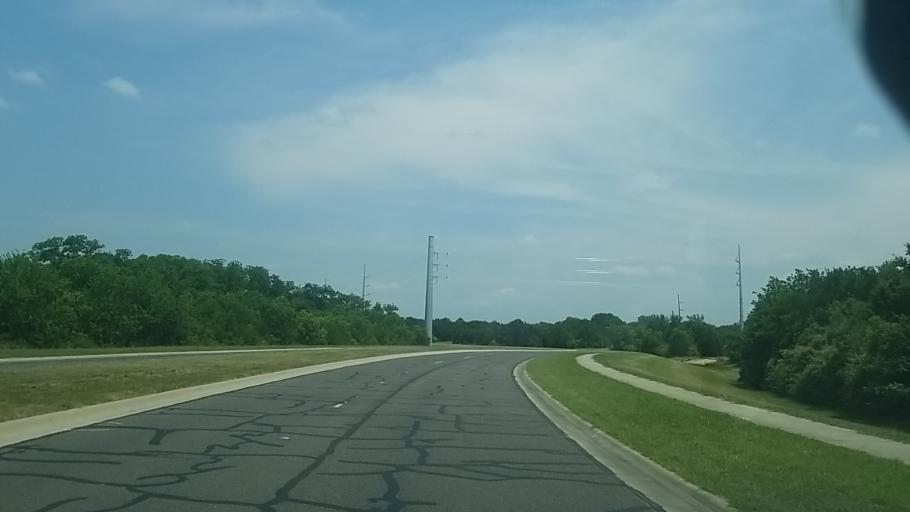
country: US
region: Texas
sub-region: Denton County
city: Denton
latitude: 33.2046
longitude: -97.1020
